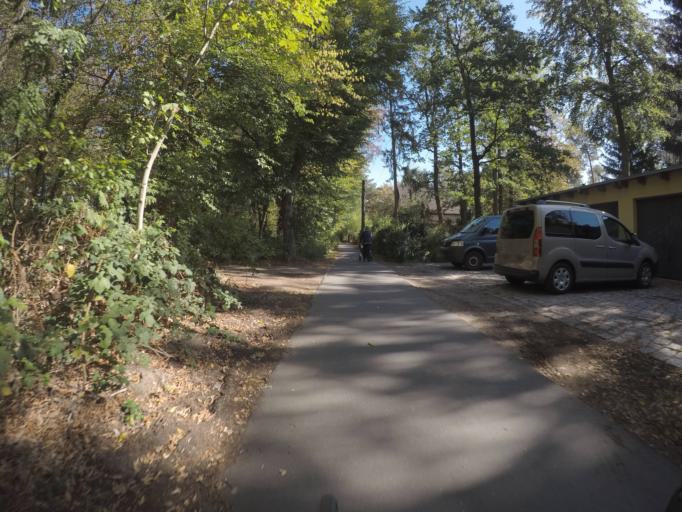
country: DE
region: Berlin
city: Falkenhagener Feld
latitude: 52.5996
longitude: 13.1418
